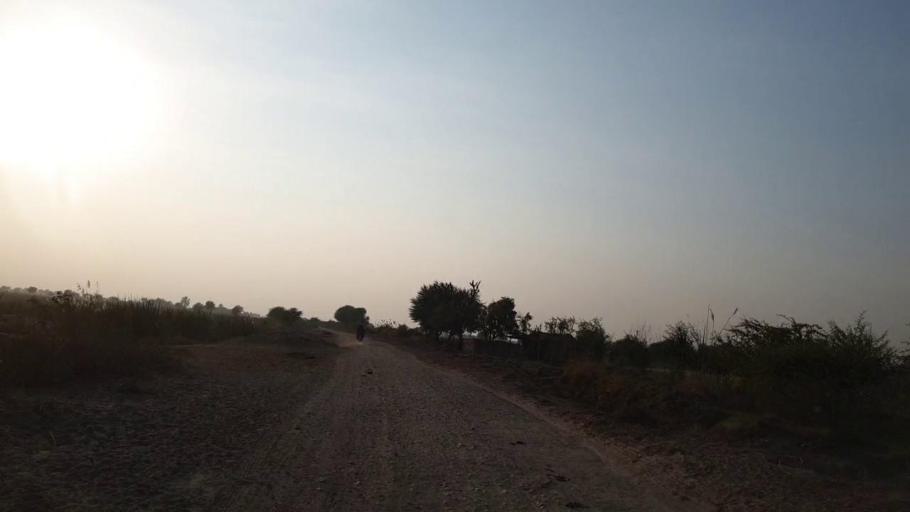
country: PK
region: Sindh
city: Pithoro
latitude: 25.6544
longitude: 69.2217
